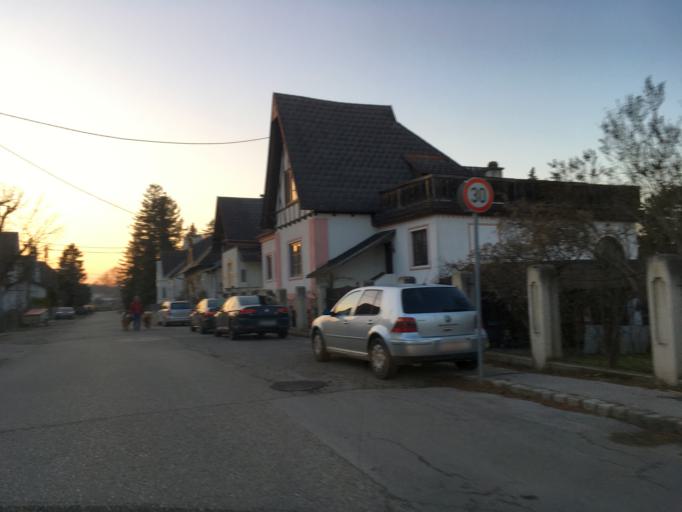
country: AT
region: Lower Austria
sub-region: Politischer Bezirk Tulln
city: Wordern
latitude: 48.3322
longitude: 16.2086
